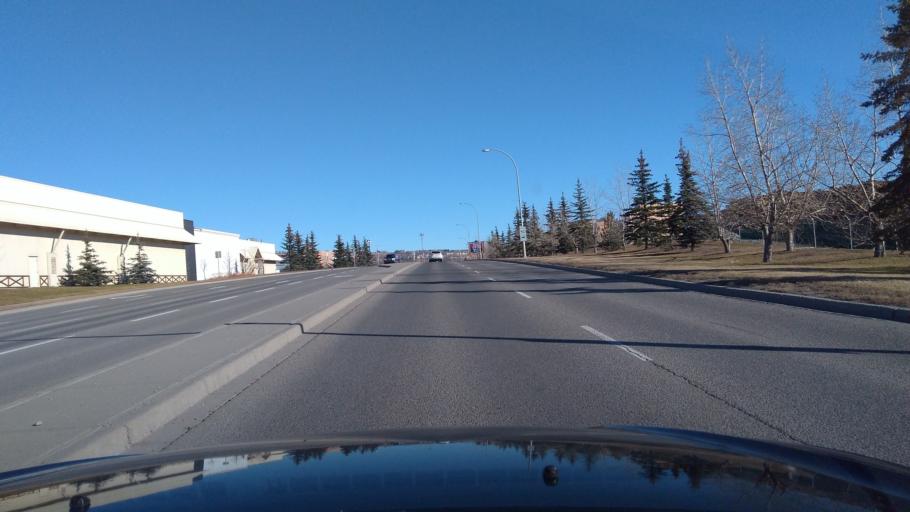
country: CA
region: Alberta
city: Cochrane
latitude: 51.1831
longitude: -114.4779
